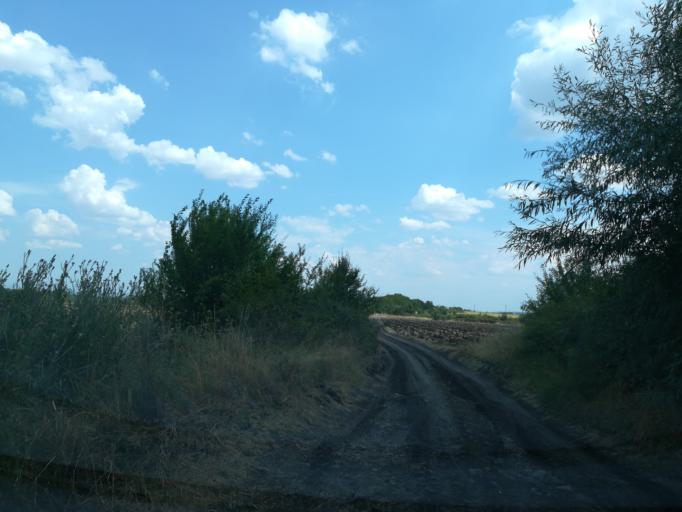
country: BG
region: Khaskovo
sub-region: Obshtina Mineralni Bani
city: Mineralni Bani
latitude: 42.0072
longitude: 25.2170
